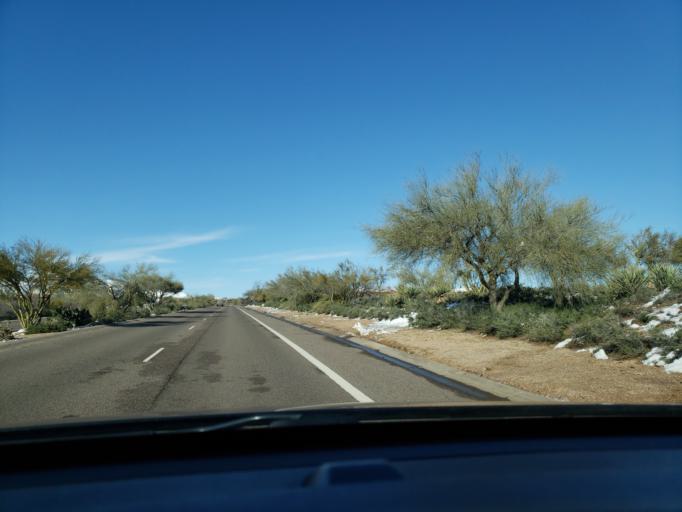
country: US
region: Arizona
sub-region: Maricopa County
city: Carefree
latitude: 33.8329
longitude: -111.8538
